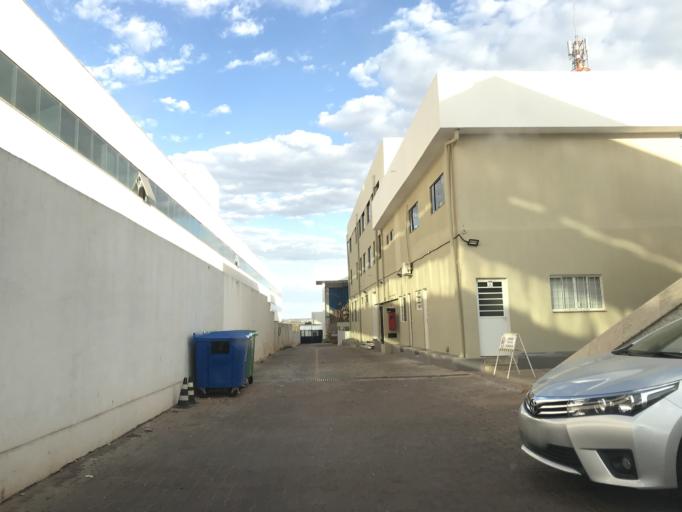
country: BR
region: Federal District
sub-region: Brasilia
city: Brasilia
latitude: -15.8292
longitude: -47.9042
